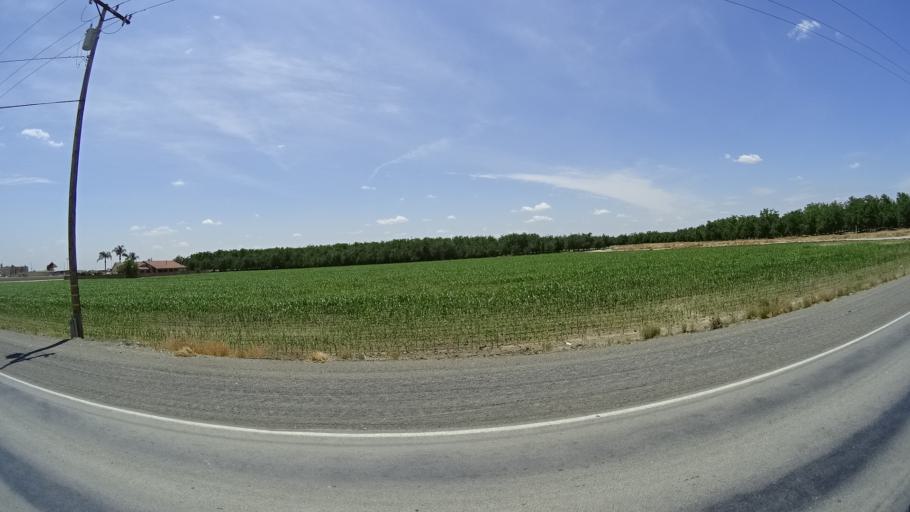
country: US
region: California
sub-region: Kings County
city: Home Garden
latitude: 36.2983
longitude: -119.6608
